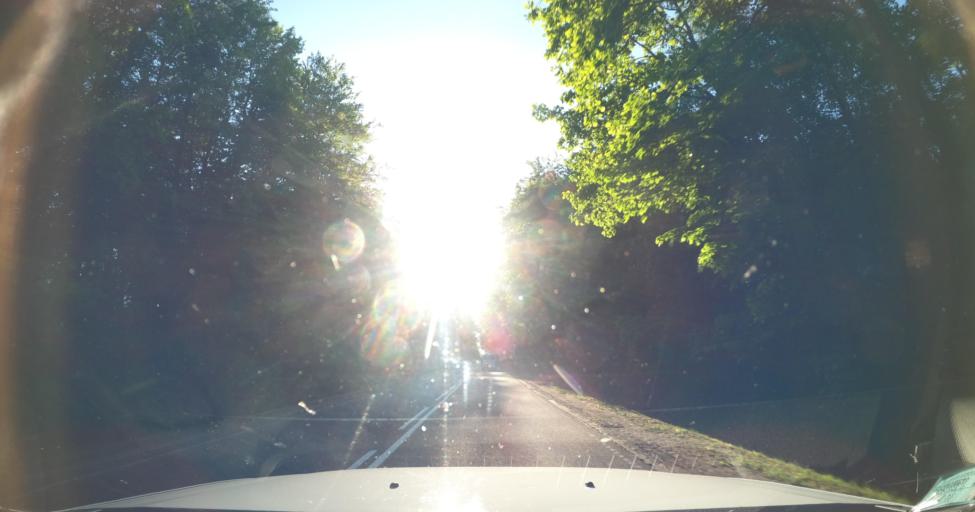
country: PL
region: Pomeranian Voivodeship
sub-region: Powiat kartuski
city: Kartuzy
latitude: 54.3250
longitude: 18.2367
